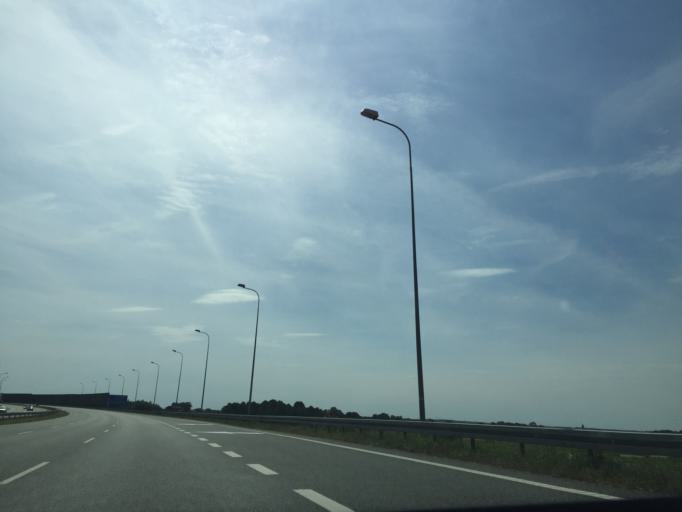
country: PL
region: Silesian Voivodeship
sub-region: Powiat tarnogorski
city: Wieszowa
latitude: 50.3692
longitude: 18.7361
